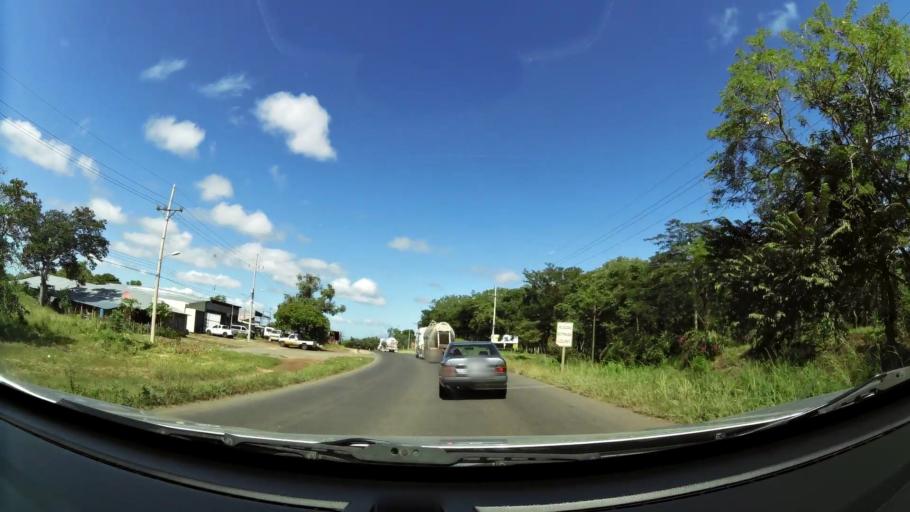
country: CR
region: Guanacaste
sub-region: Canton de Canas
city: Canas
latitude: 10.4126
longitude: -85.0854
